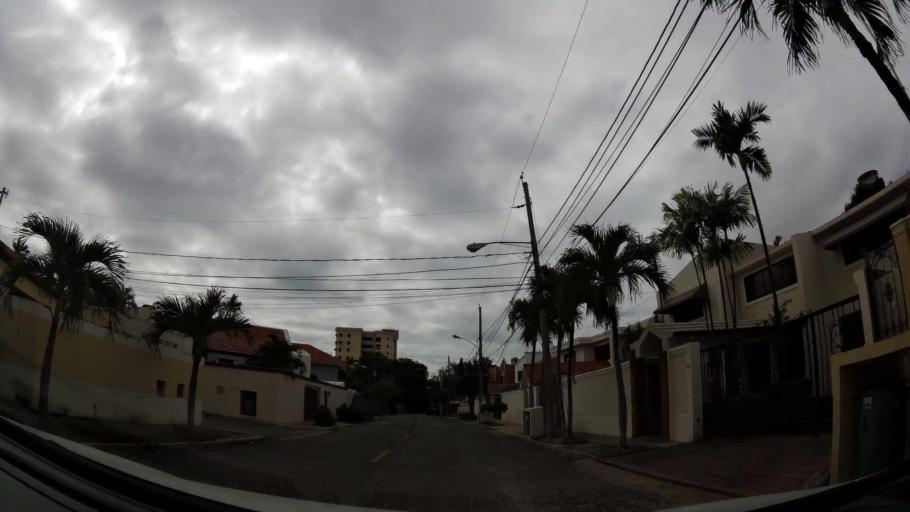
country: DO
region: Nacional
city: Bella Vista
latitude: 18.4507
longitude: -69.9431
